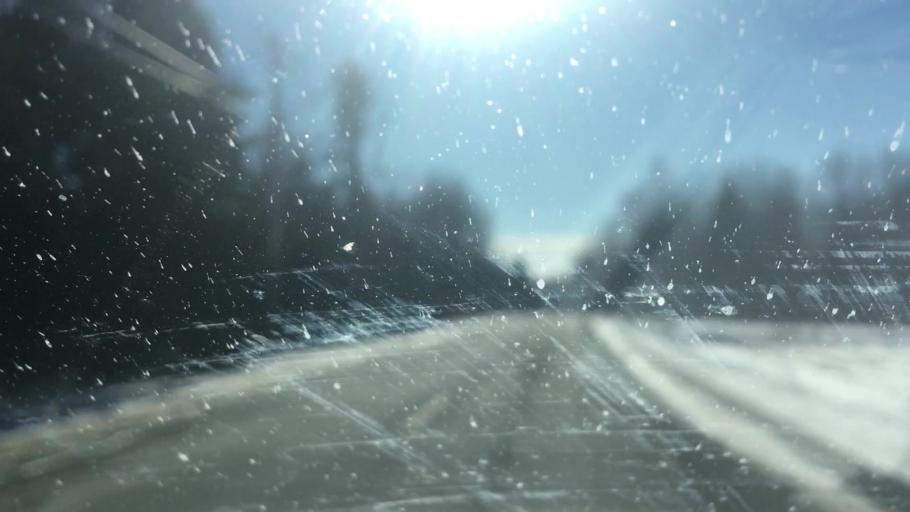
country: US
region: Maine
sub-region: Hancock County
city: Sedgwick
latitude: 44.3887
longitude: -68.6429
